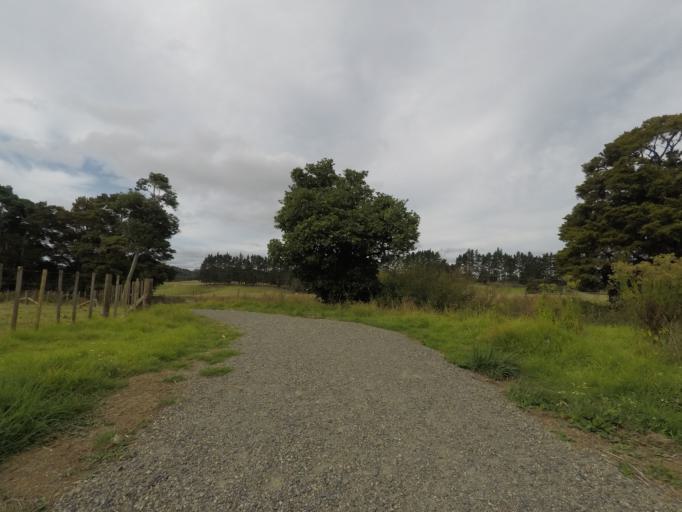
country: NZ
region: Northland
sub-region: Whangarei
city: Whangarei
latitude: -35.6758
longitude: 174.3325
